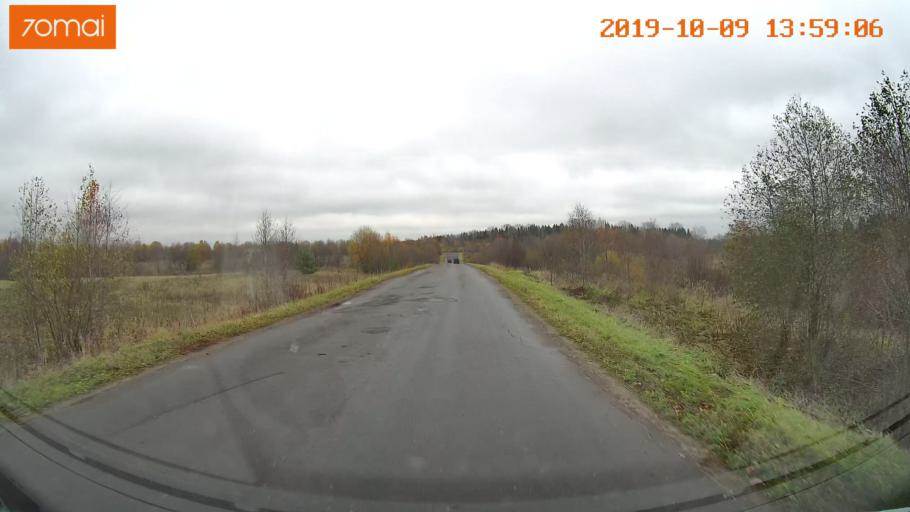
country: RU
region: Kostroma
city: Buy
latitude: 58.4349
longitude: 41.3178
